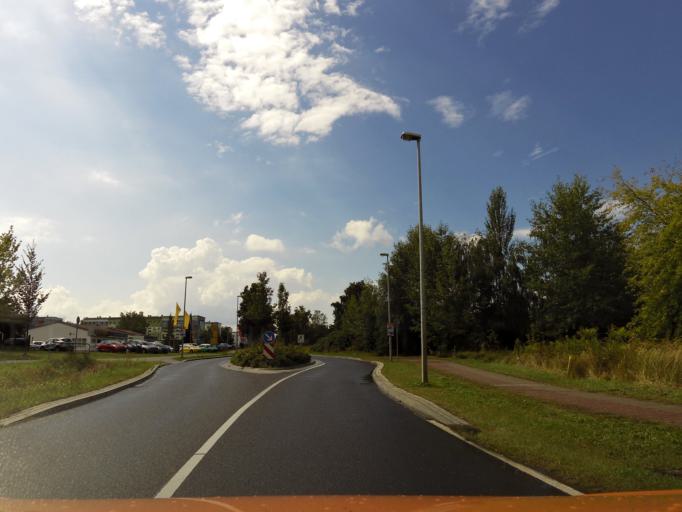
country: DE
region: Brandenburg
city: Ketzin
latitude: 52.4828
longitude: 12.8516
